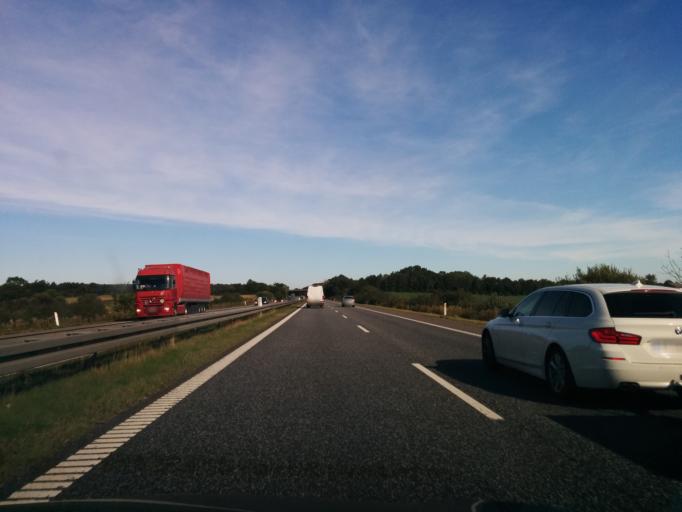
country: DK
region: South Denmark
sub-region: Fredericia Kommune
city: Taulov
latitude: 55.5821
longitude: 9.5753
